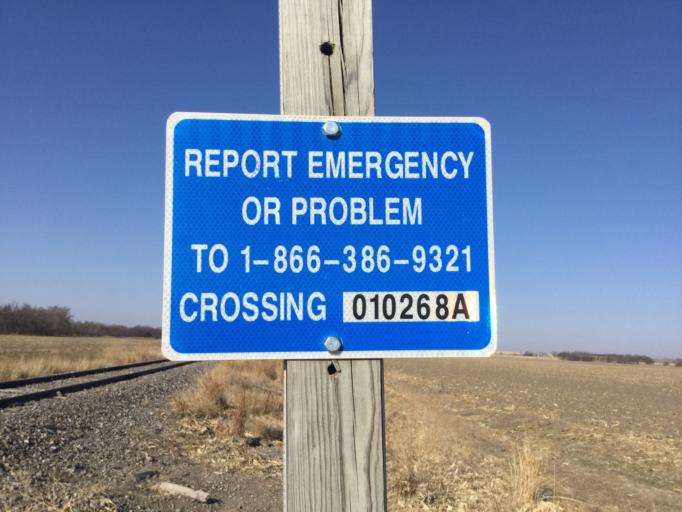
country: US
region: Kansas
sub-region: Rush County
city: La Crosse
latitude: 38.4702
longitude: -99.2167
